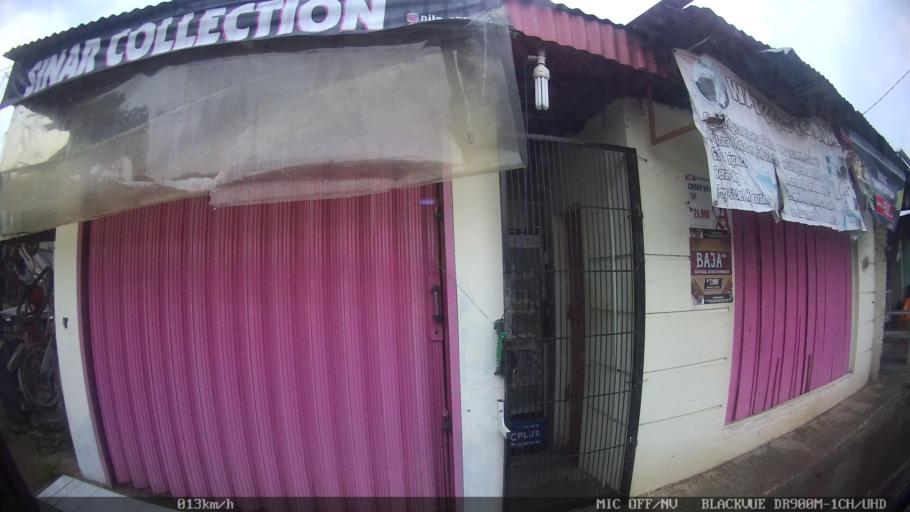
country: ID
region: Lampung
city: Bandarlampung
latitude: -5.4393
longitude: 105.2756
